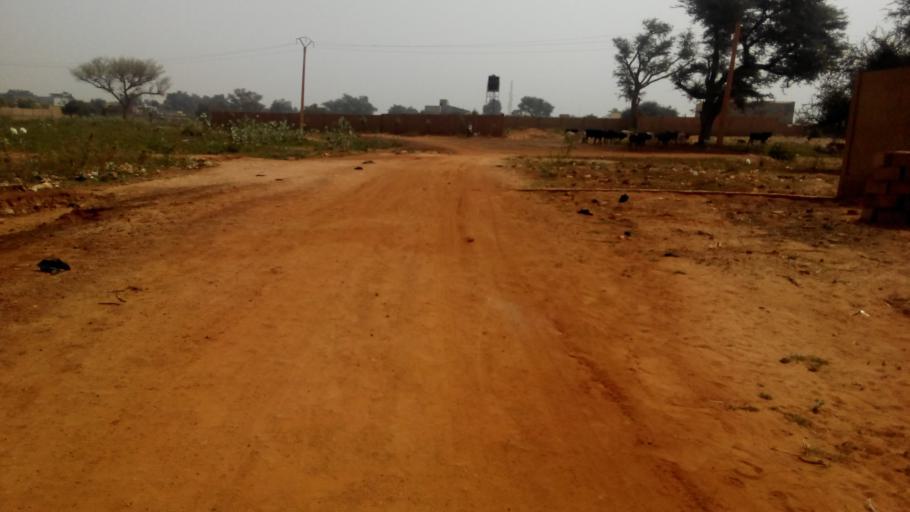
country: NE
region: Niamey
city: Niamey
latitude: 13.5419
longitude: 2.0590
